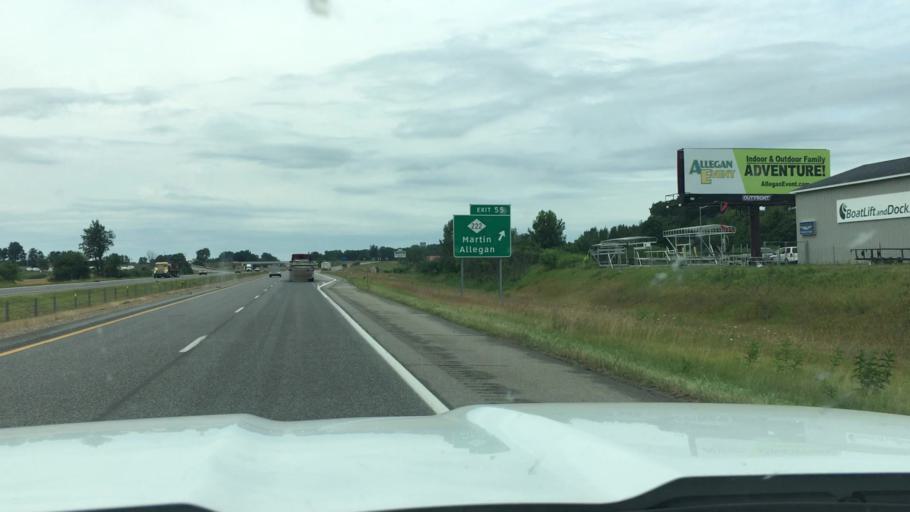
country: US
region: Michigan
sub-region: Allegan County
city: Otsego
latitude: 42.5430
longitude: -85.6613
